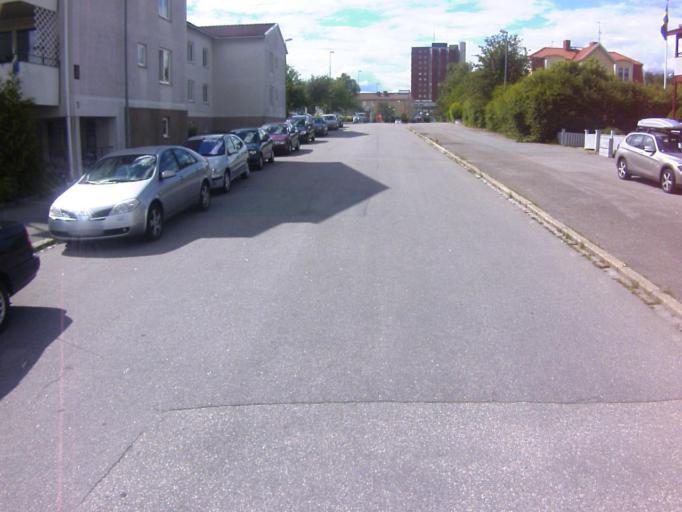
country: SE
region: Soedermanland
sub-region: Eskilstuna Kommun
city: Eskilstuna
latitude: 59.3550
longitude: 16.5043
